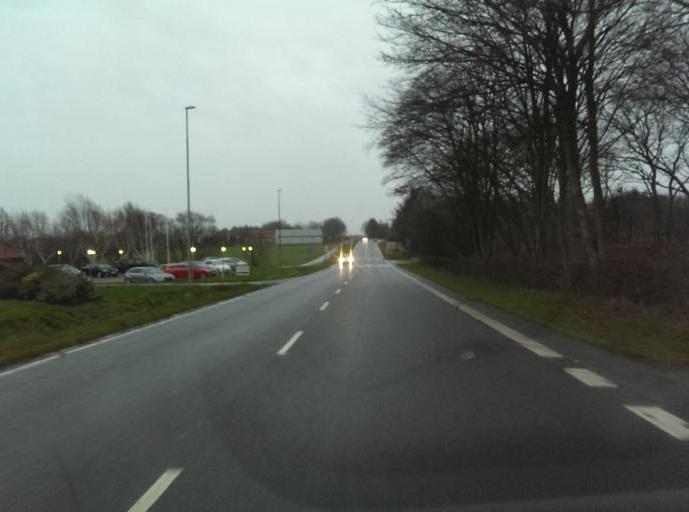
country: DK
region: South Denmark
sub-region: Esbjerg Kommune
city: Tjaereborg
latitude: 55.4982
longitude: 8.5309
